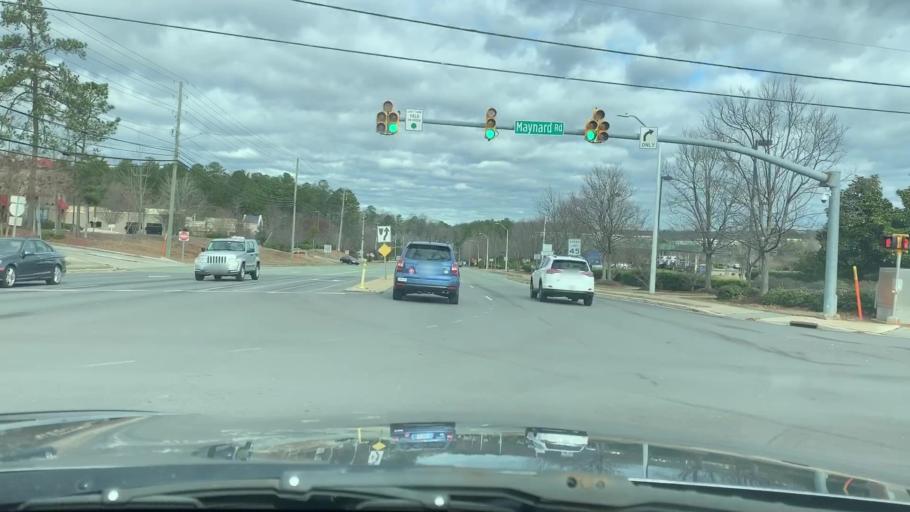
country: US
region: North Carolina
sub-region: Wake County
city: Cary
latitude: 35.8027
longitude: -78.7829
